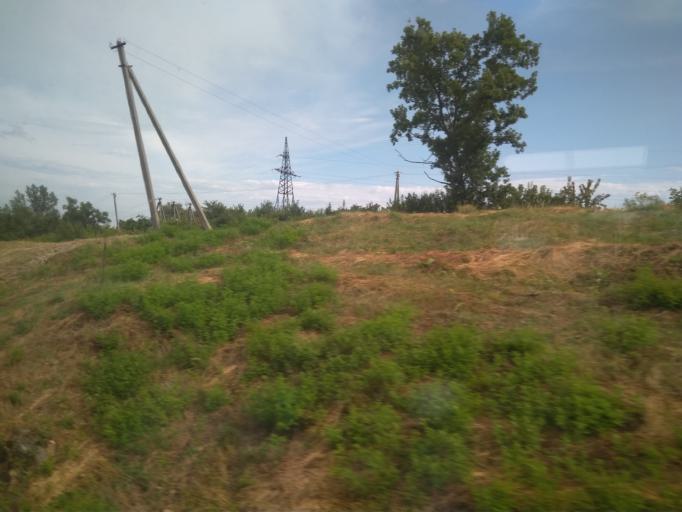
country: RU
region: Krasnodarskiy
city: Pshekhskaya
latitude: 44.7159
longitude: 39.8008
